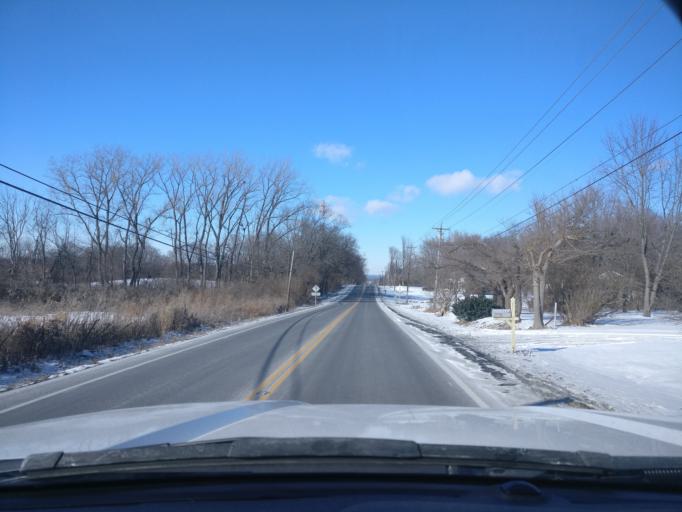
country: US
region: Ohio
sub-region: Warren County
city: Hunter
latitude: 39.5226
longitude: -84.2766
